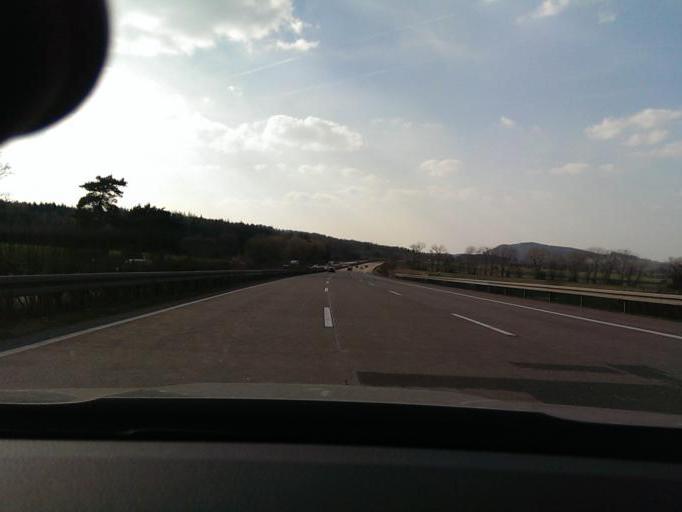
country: DE
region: Thuringia
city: Mechterstadt
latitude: 50.9221
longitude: 10.5260
